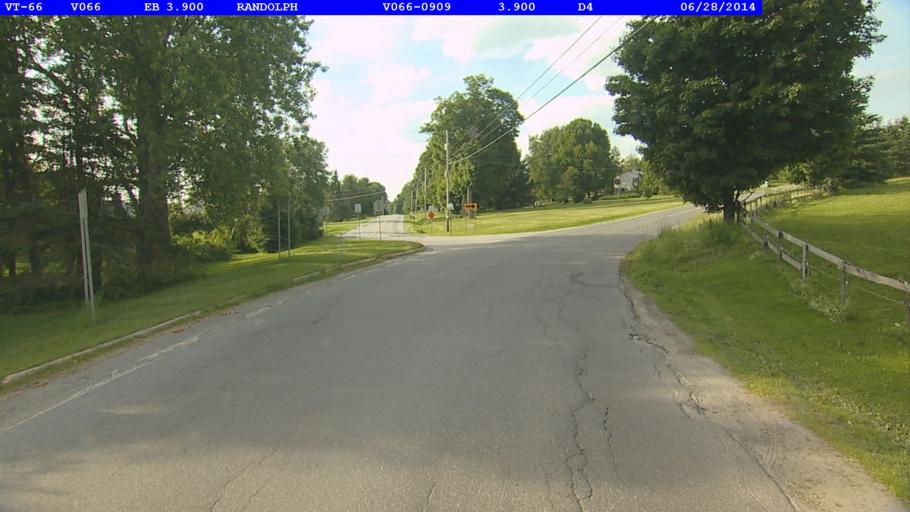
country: US
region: Vermont
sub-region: Orange County
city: Randolph
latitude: 43.9488
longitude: -72.6085
